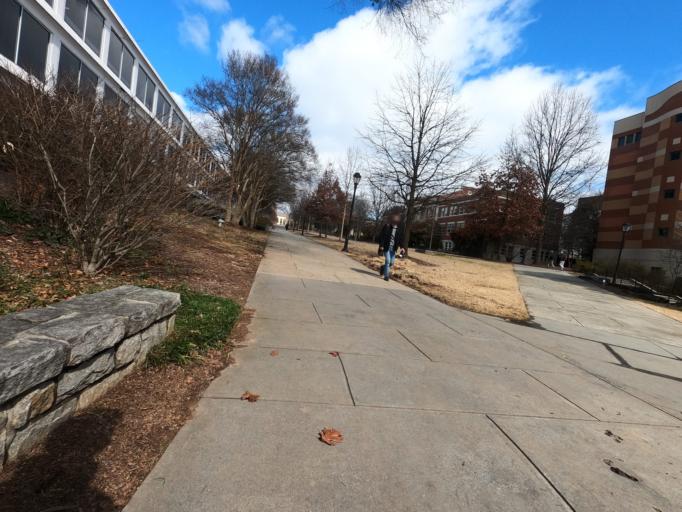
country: US
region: Georgia
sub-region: Clarke County
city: Athens
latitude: 33.9436
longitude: -83.3753
